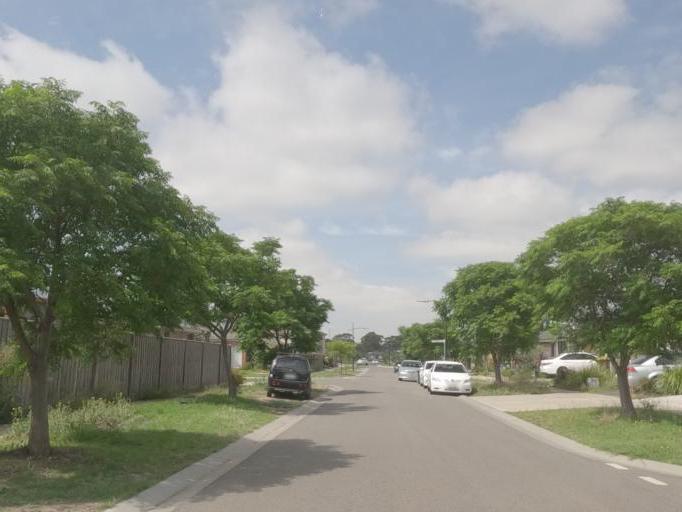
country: AU
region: Victoria
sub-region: Hume
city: Greenvale
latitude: -37.6259
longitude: 144.8749
